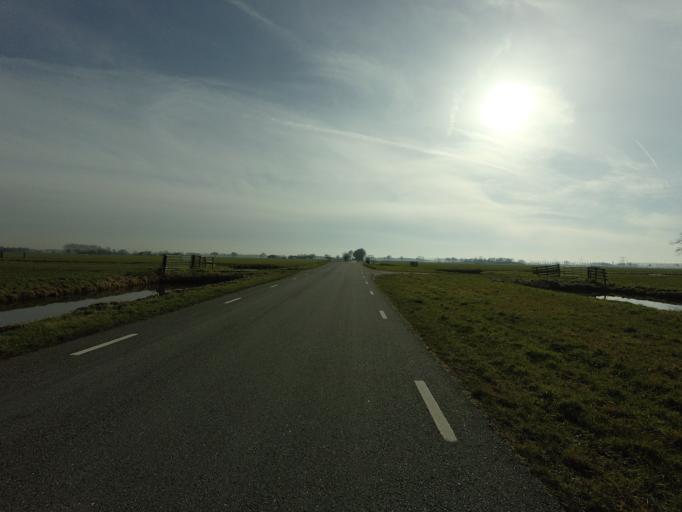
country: NL
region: South Holland
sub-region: Gemeente Hardinxveld-Giessendam
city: Neder-Hardinxveld
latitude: 51.8688
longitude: 4.8125
